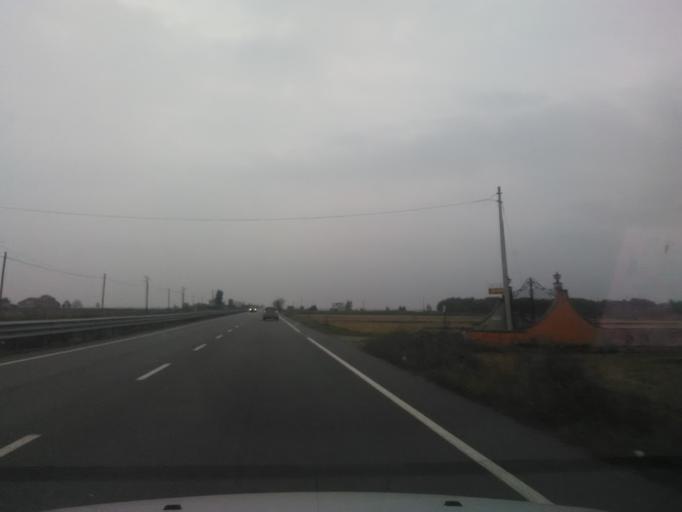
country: IT
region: Piedmont
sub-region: Provincia di Vercelli
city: San Germano Vercellese
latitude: 45.3521
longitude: 8.2332
